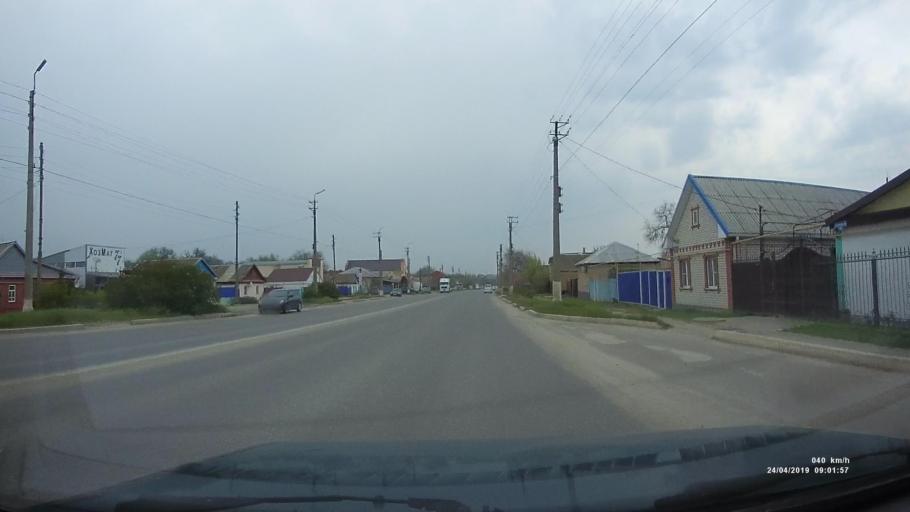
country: RU
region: Kalmykiya
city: Elista
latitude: 46.3124
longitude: 44.2292
